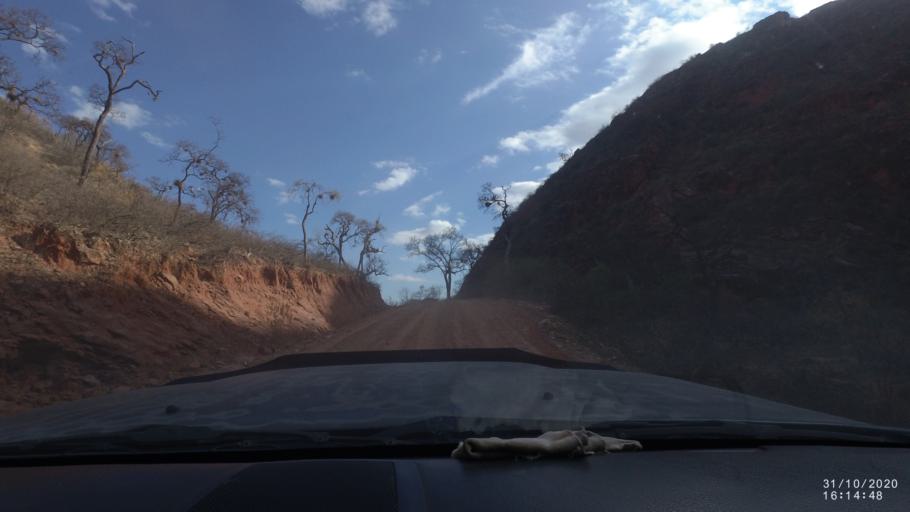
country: BO
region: Chuquisaca
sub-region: Provincia Zudanez
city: Mojocoya
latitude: -18.3854
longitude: -64.6146
